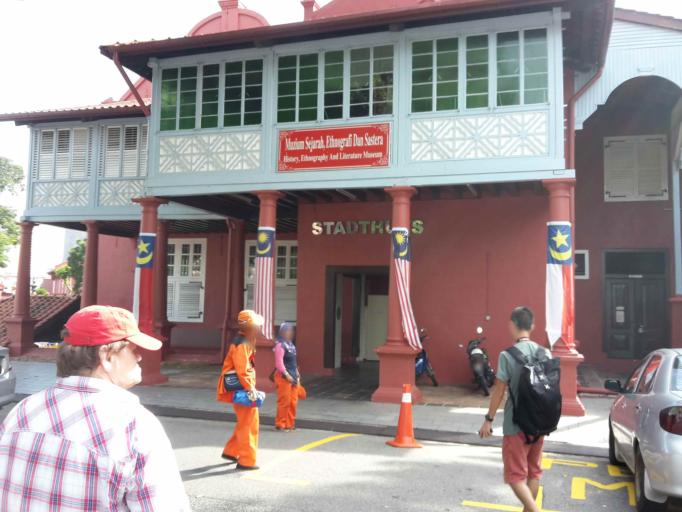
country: MY
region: Melaka
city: Malacca
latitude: 2.1940
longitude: 102.2487
